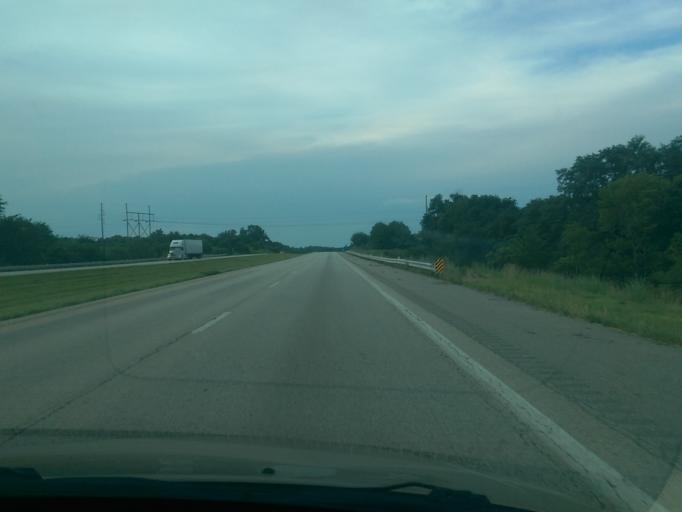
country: US
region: Missouri
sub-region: Andrew County
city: Country Club Village
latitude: 39.8411
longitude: -94.8052
